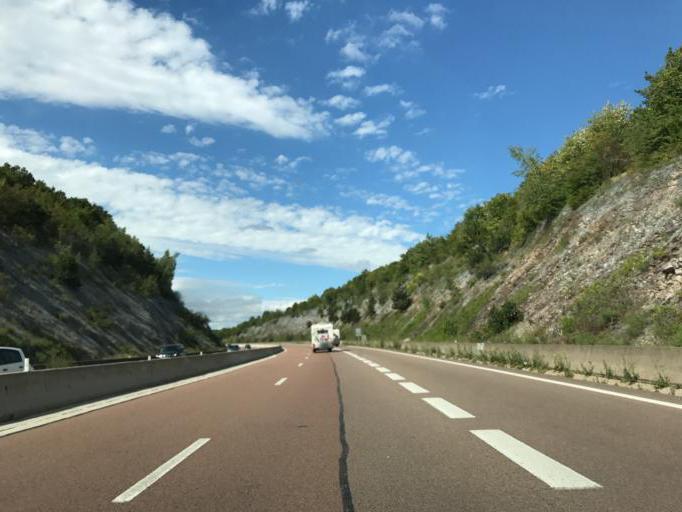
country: FR
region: Bourgogne
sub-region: Departement de la Cote-d'Or
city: Savigny-les-Beaune
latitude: 47.0718
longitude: 4.7658
